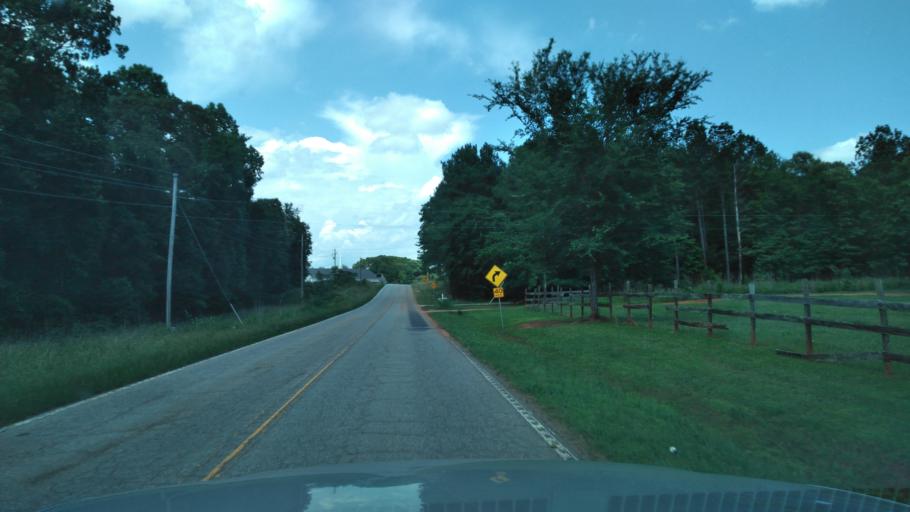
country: US
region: South Carolina
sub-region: Laurens County
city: Laurens
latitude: 34.4914
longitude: -82.1135
